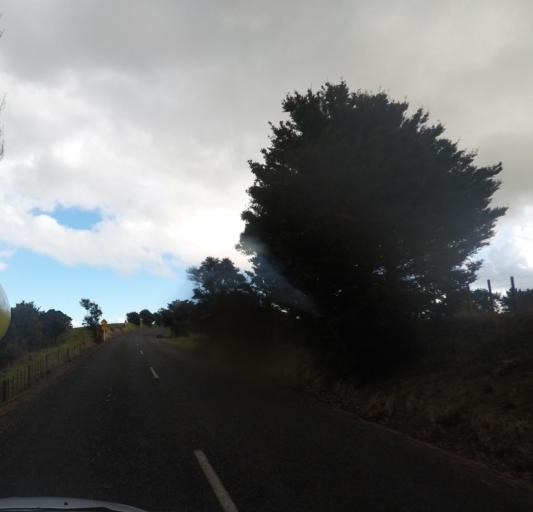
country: NZ
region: Auckland
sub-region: Auckland
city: Warkworth
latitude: -36.3748
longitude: 174.7613
